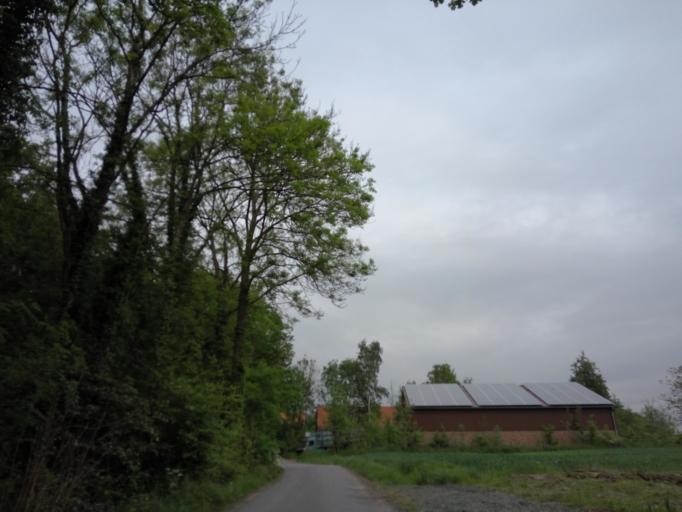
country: DE
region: North Rhine-Westphalia
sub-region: Regierungsbezirk Munster
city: Muenster
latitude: 51.9786
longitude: 7.5868
